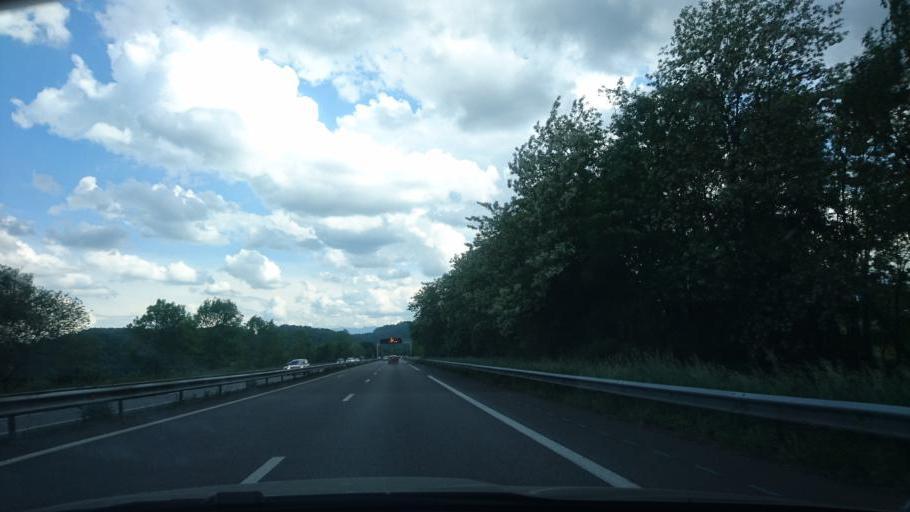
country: FR
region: Midi-Pyrenees
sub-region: Departement des Hautes-Pyrenees
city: Tournay
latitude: 43.1924
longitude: 0.2190
